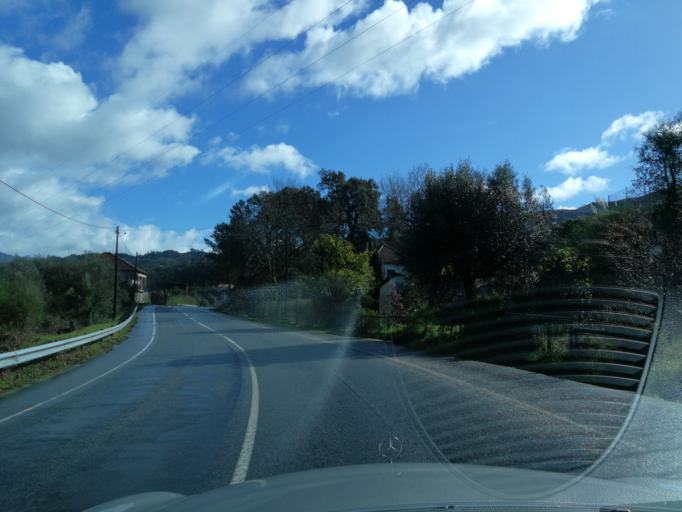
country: PT
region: Braga
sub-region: Terras de Bouro
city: Antas
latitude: 41.8352
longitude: -8.2975
